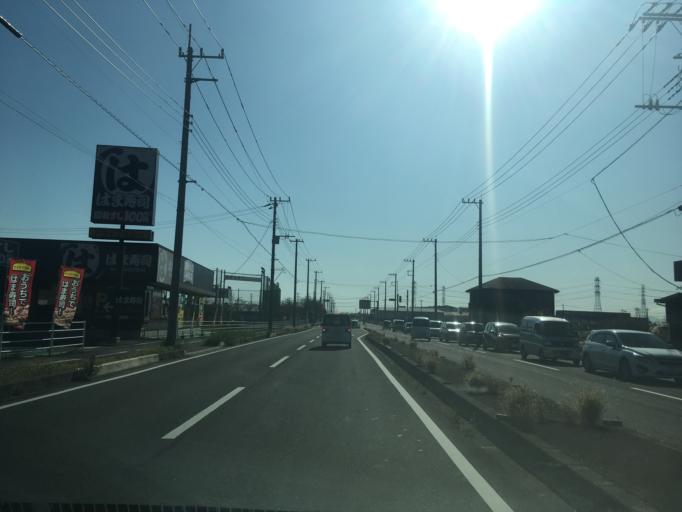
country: JP
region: Saitama
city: Kawagoe
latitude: 35.9305
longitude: 139.4678
